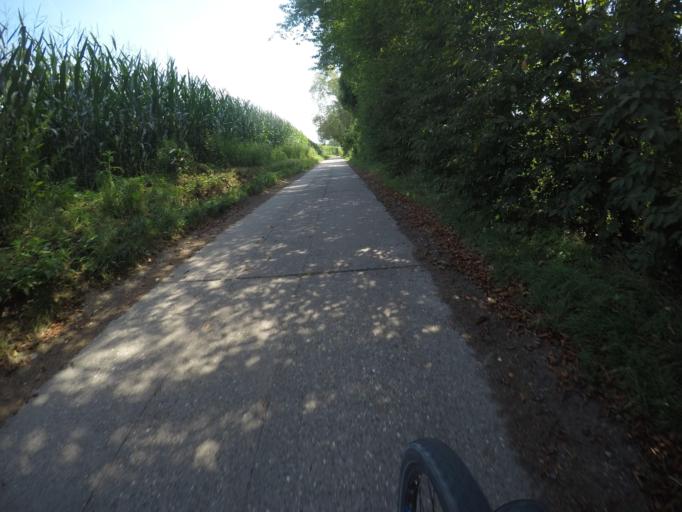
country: DE
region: Baden-Wuerttemberg
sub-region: Karlsruhe Region
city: Gondelsheim
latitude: 49.0563
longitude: 8.6653
